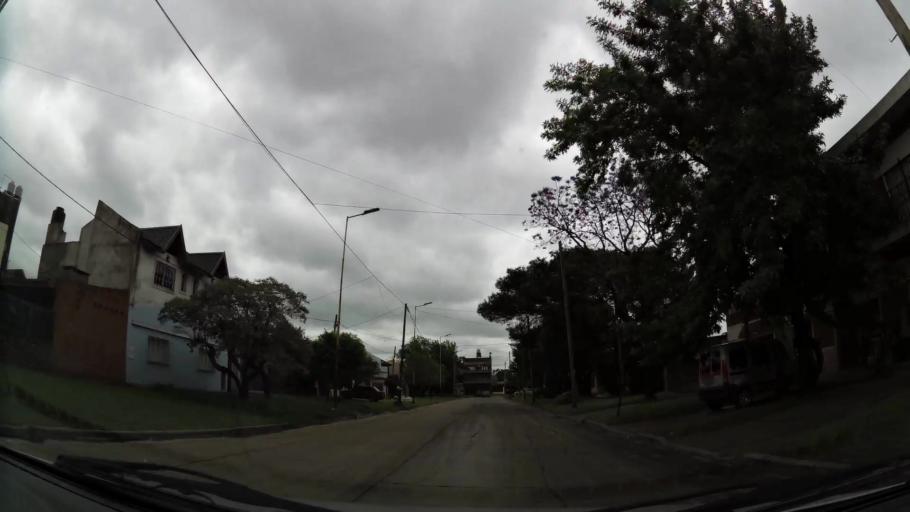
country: AR
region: Buenos Aires
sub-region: Partido de Lomas de Zamora
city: Lomas de Zamora
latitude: -34.7434
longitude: -58.3737
